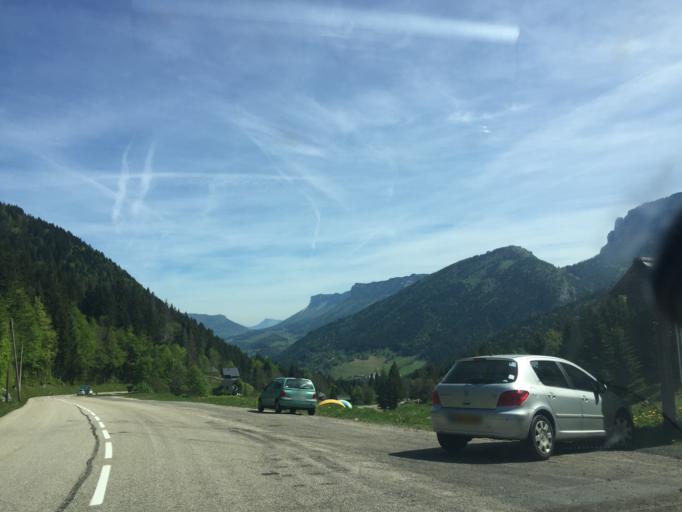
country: FR
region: Rhone-Alpes
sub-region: Departement de l'Isere
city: Saint-Hilaire
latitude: 45.3657
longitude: 5.8342
